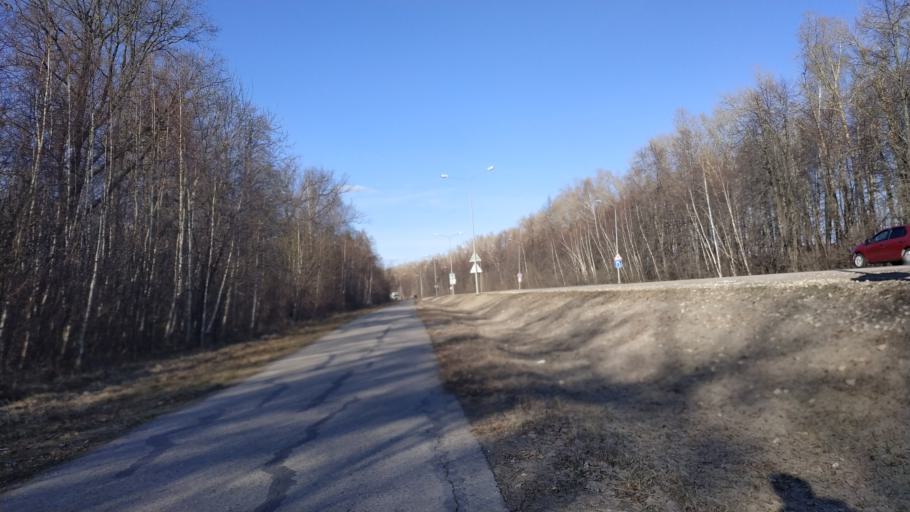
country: RU
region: Chuvashia
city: Ishley
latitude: 56.1271
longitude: 47.0668
